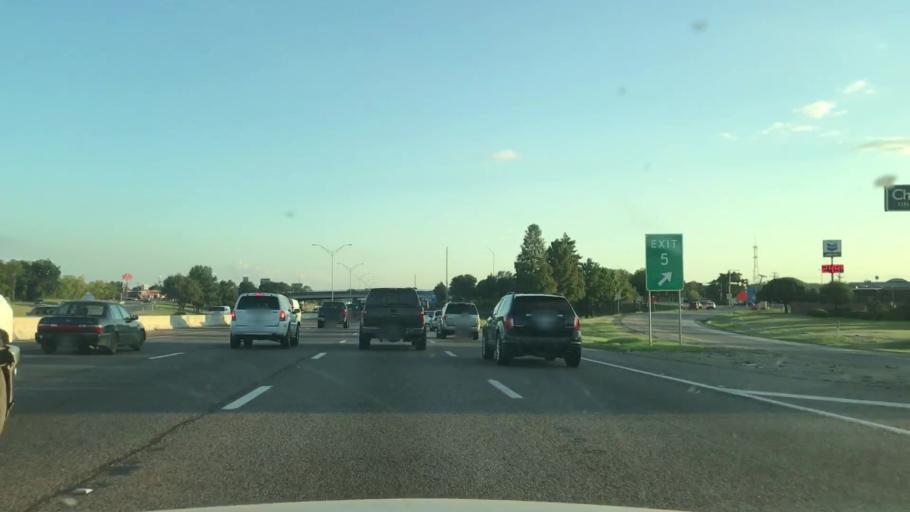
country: US
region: Texas
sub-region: Dallas County
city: Mesquite
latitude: 32.7842
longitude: -96.6246
